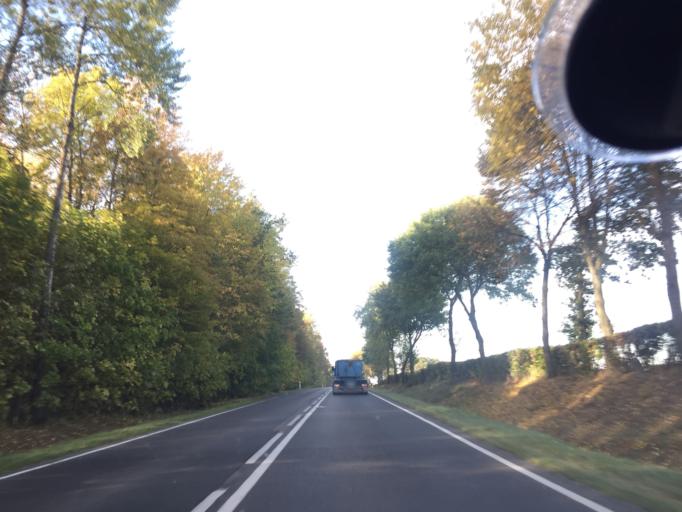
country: PL
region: Warmian-Masurian Voivodeship
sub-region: Powiat lidzbarski
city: Lidzbark Warminski
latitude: 54.1727
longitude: 20.6911
